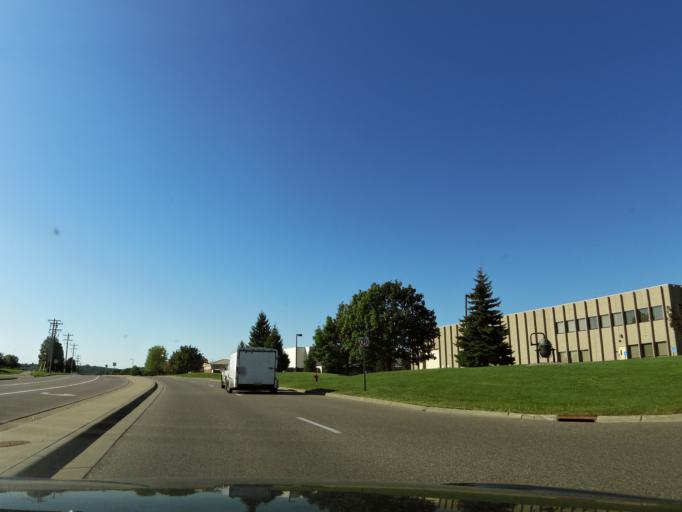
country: US
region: Minnesota
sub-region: Scott County
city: Savage
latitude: 44.7461
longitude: -93.3235
